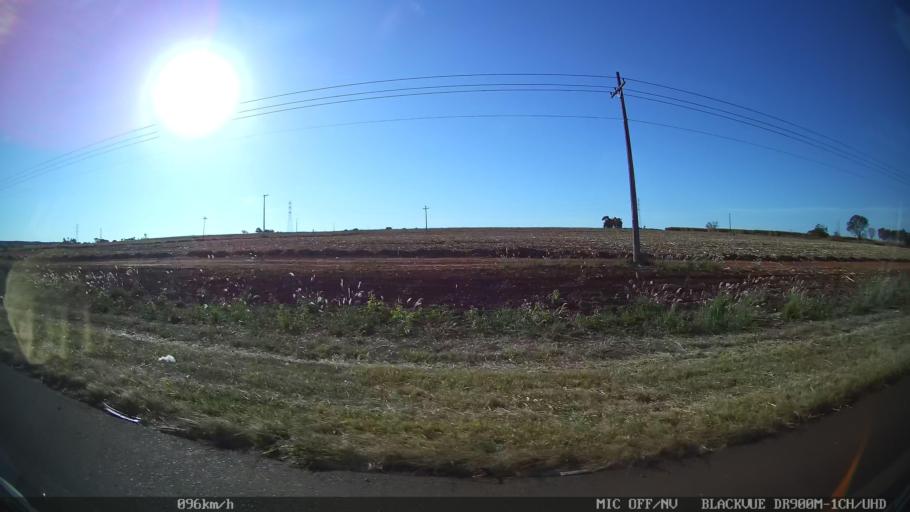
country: BR
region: Sao Paulo
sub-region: Olimpia
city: Olimpia
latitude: -20.7104
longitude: -48.9749
